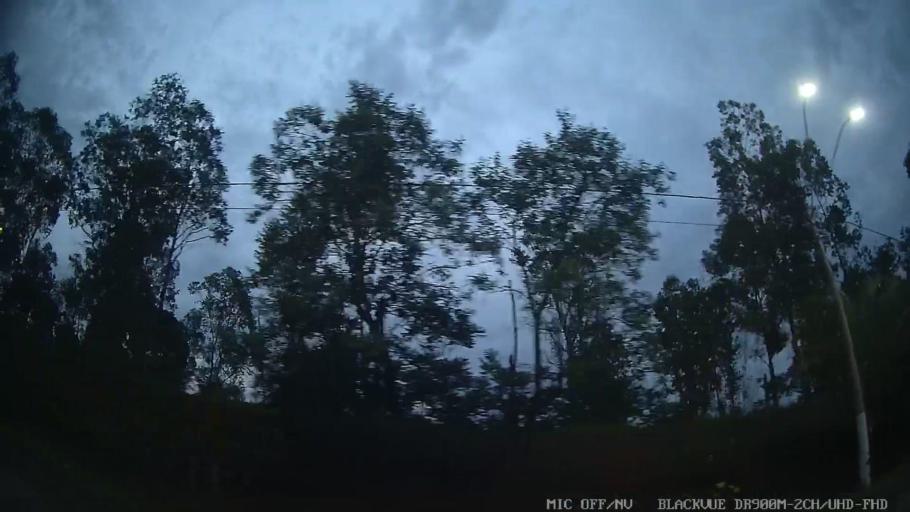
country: BR
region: Sao Paulo
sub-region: Itatiba
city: Itatiba
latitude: -22.8667
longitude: -46.7905
